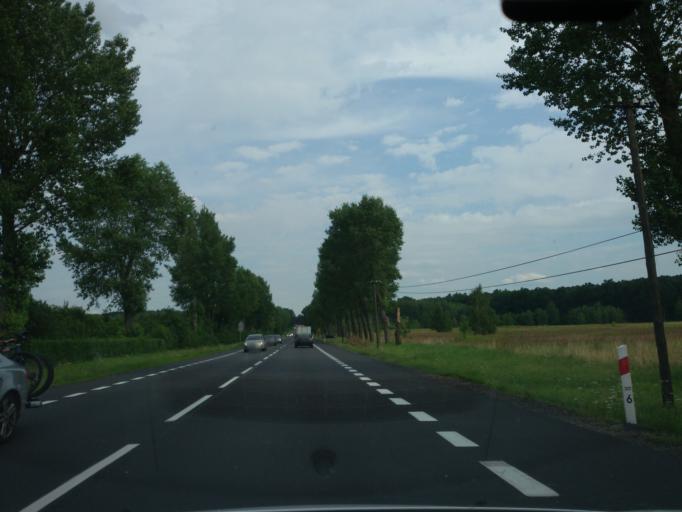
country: PL
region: Lubusz
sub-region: Powiat nowosolski
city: Nowe Miasteczko
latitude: 51.6867
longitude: 15.7446
